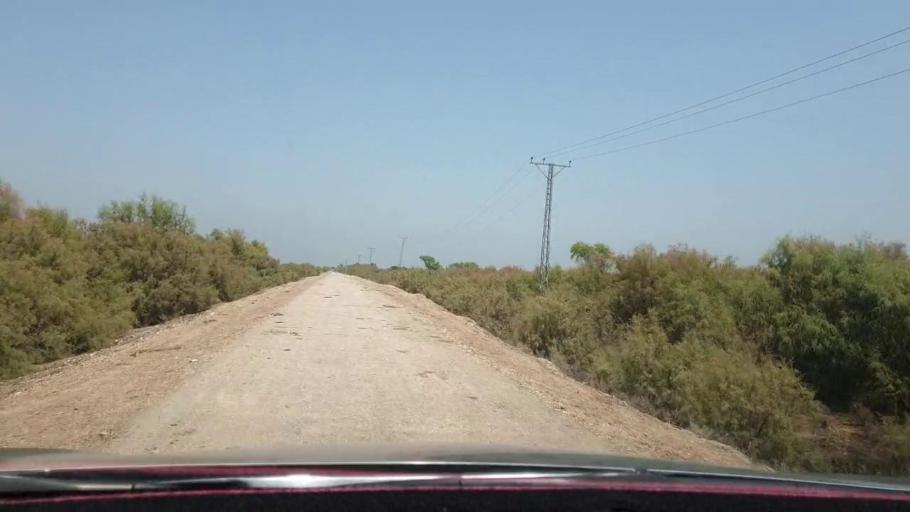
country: PK
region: Sindh
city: Warah
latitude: 27.4044
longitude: 67.6917
